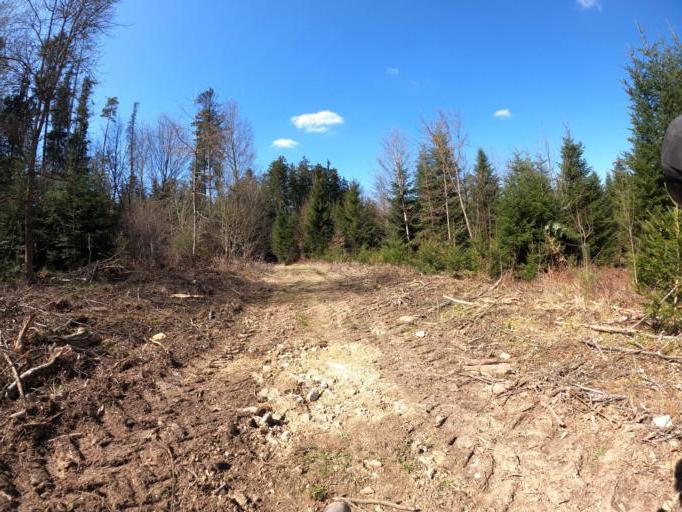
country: DE
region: Baden-Wuerttemberg
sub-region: Tuebingen Region
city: Haigerloch
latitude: 48.4197
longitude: 8.7792
